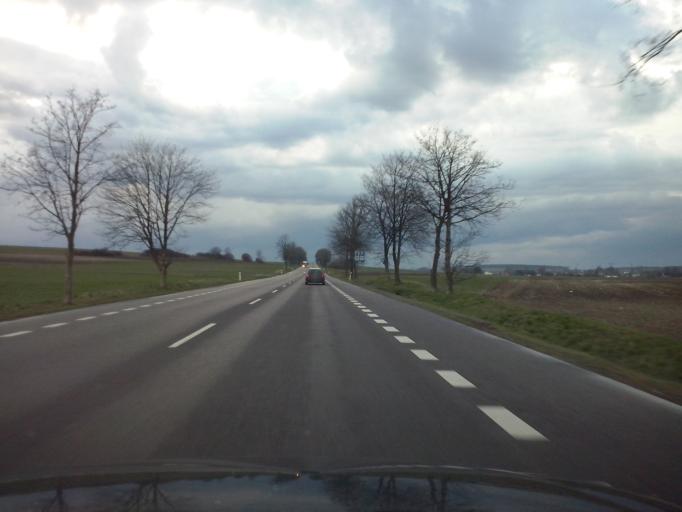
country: PL
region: Lublin Voivodeship
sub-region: Chelm
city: Chelm
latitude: 51.1664
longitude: 23.3699
